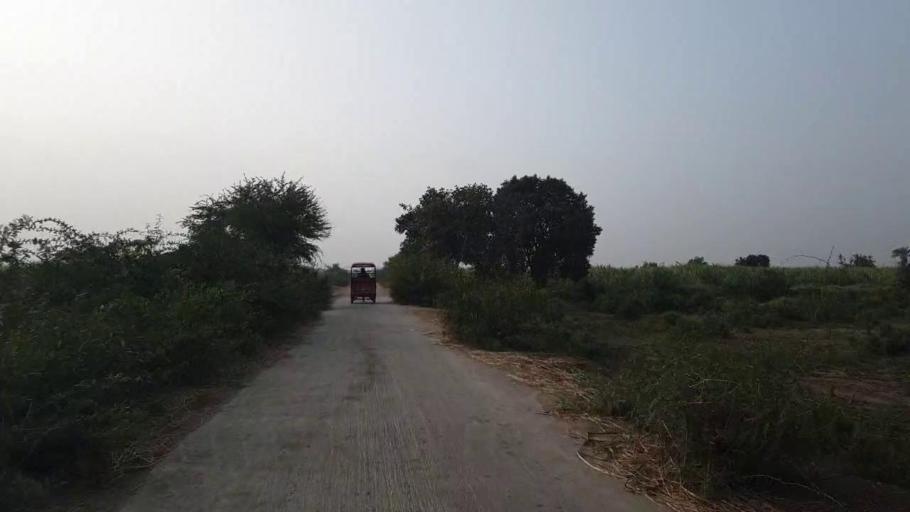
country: PK
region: Sindh
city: Tando Muhammad Khan
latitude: 25.1441
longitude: 68.6038
